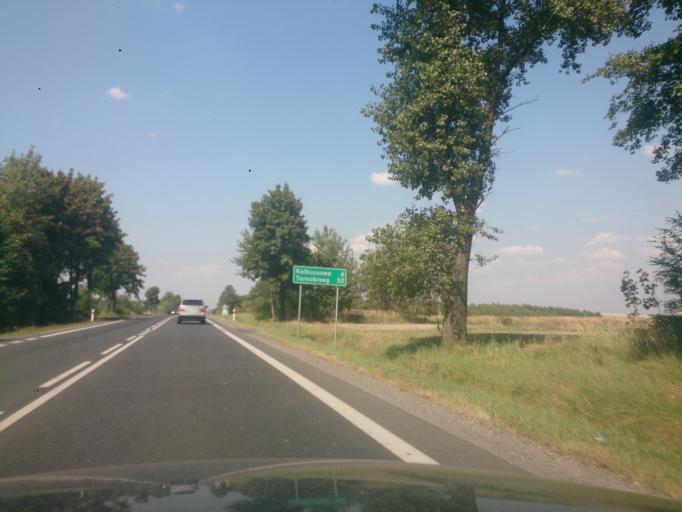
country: PL
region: Subcarpathian Voivodeship
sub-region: Powiat kolbuszowski
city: Kolbuszowa
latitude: 50.2041
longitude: 21.8328
